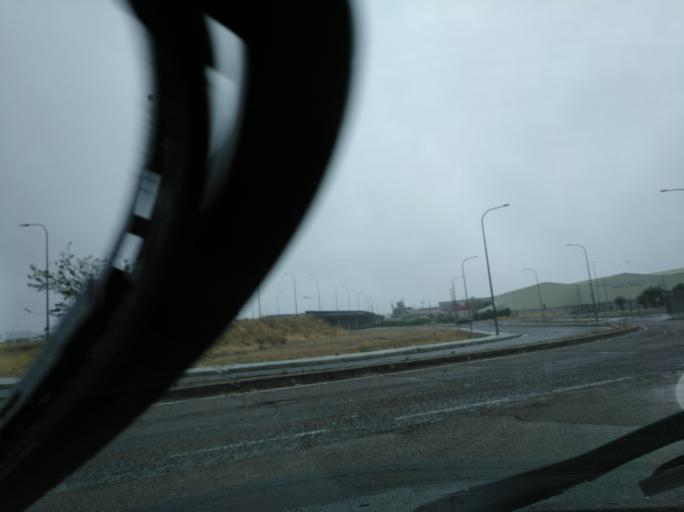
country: ES
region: Extremadura
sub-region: Provincia de Badajoz
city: Badajoz
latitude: 38.8986
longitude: -6.9915
